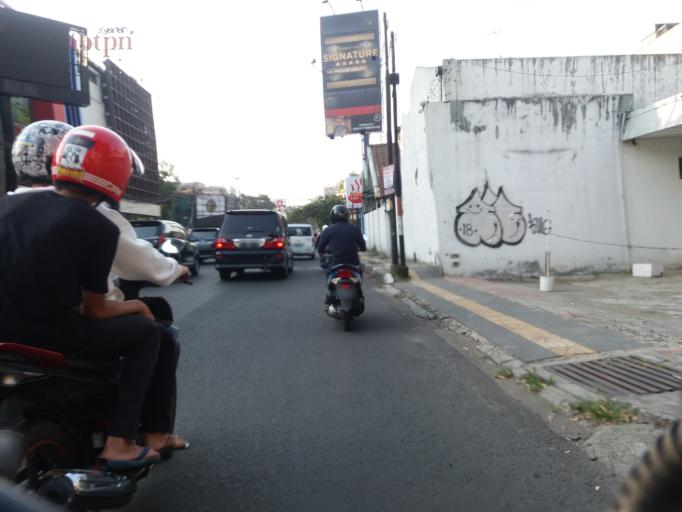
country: ID
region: West Java
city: Bandung
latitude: -6.9218
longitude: 107.6177
